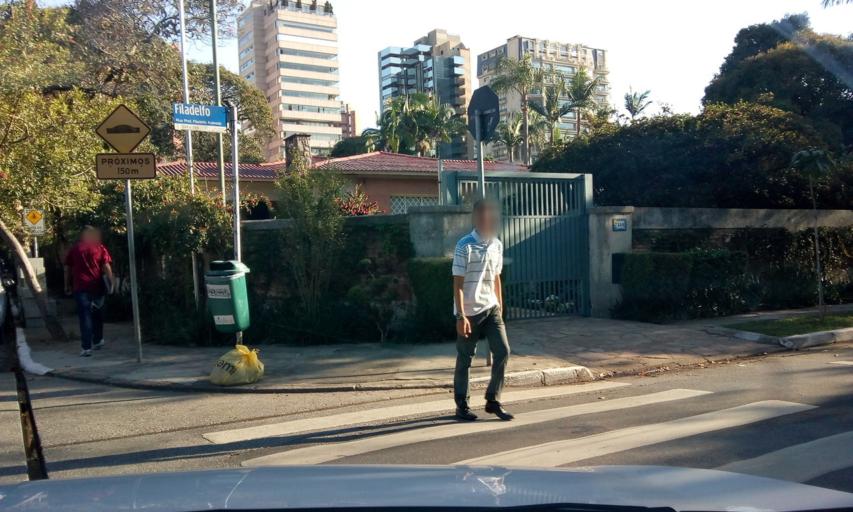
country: BR
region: Sao Paulo
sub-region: Sao Paulo
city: Sao Paulo
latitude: -23.5899
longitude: -46.6667
